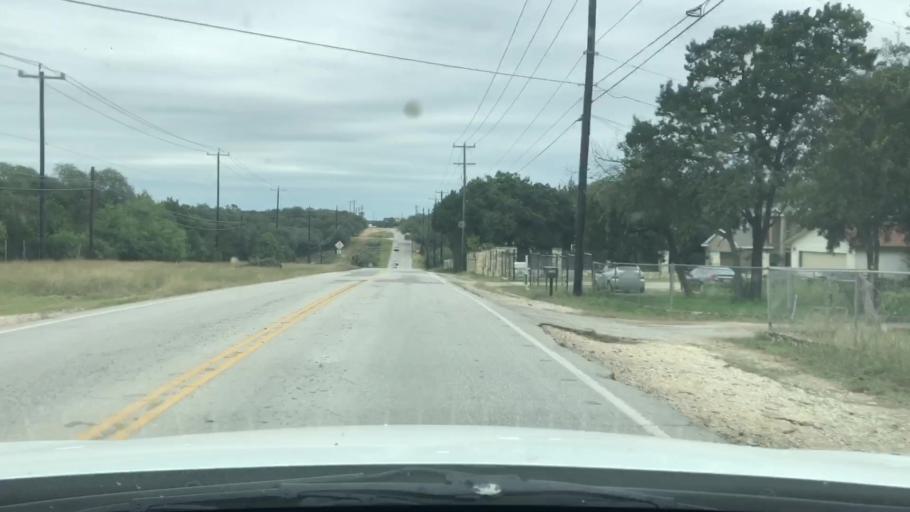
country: US
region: Texas
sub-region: Bexar County
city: Timberwood Park
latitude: 29.6473
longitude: -98.4091
